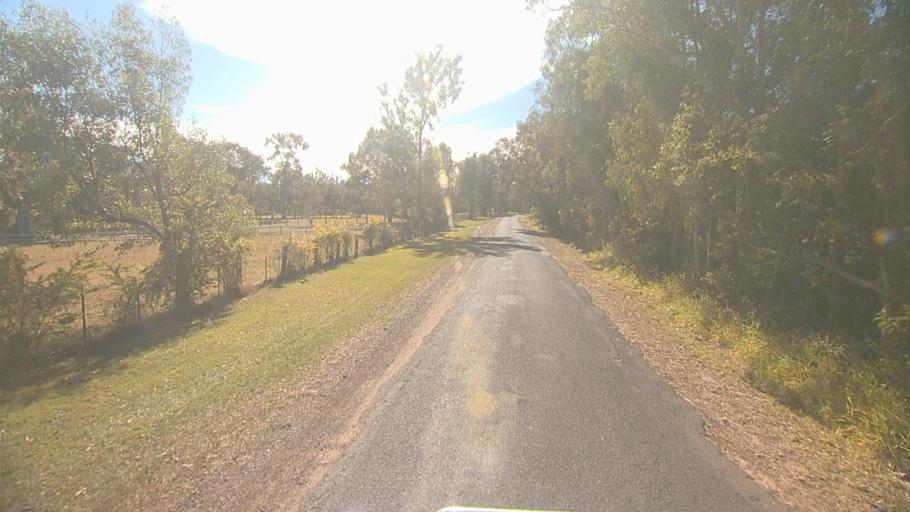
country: AU
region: Queensland
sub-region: Logan
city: Chambers Flat
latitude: -27.7879
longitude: 153.0679
